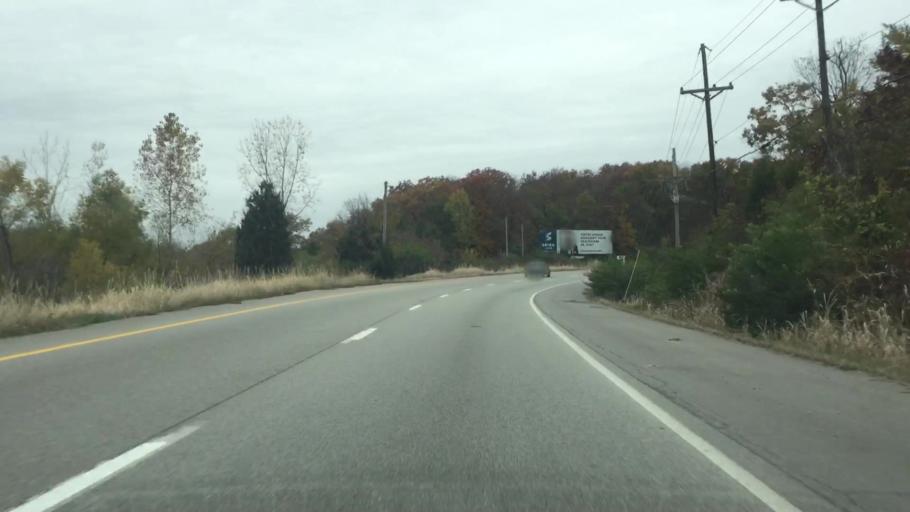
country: US
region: Missouri
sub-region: Jackson County
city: Raytown
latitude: 38.9675
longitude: -94.4342
